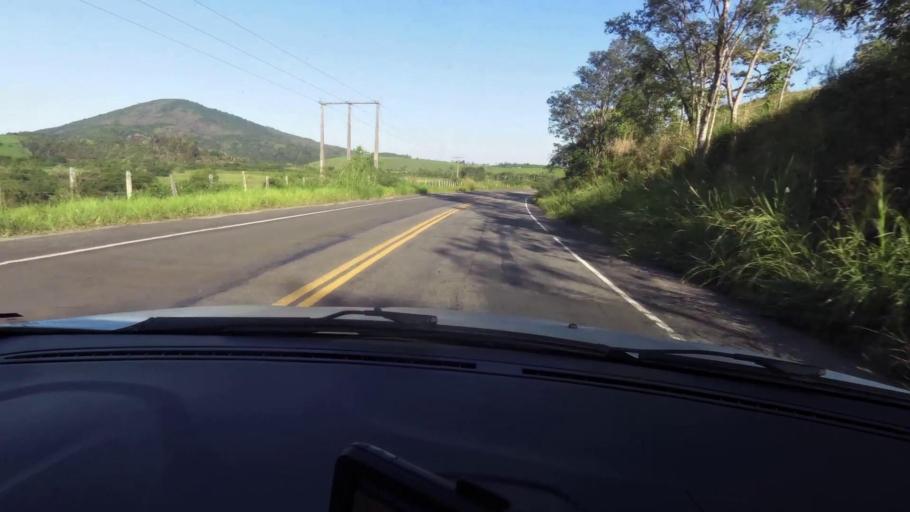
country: BR
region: Espirito Santo
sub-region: Piuma
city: Piuma
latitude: -20.7329
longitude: -40.6515
